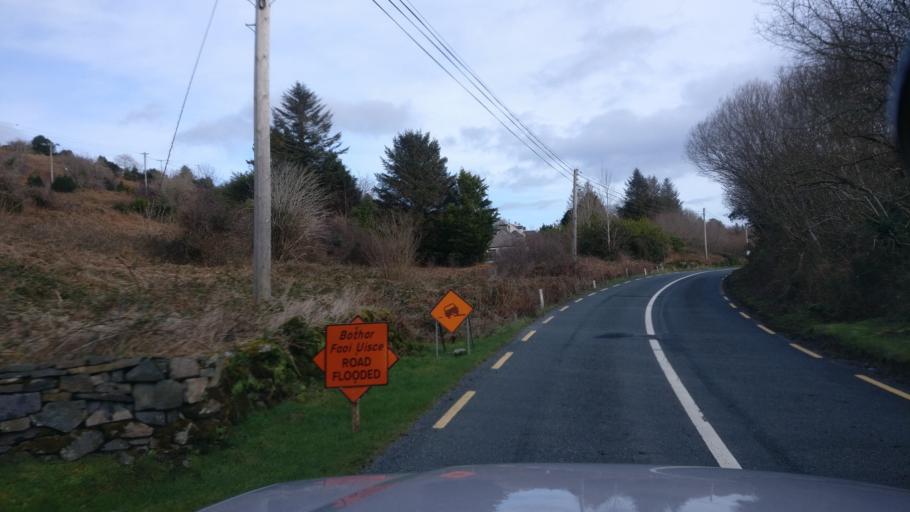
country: IE
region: Connaught
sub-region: County Galway
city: Oughterard
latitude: 53.5180
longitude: -9.4351
